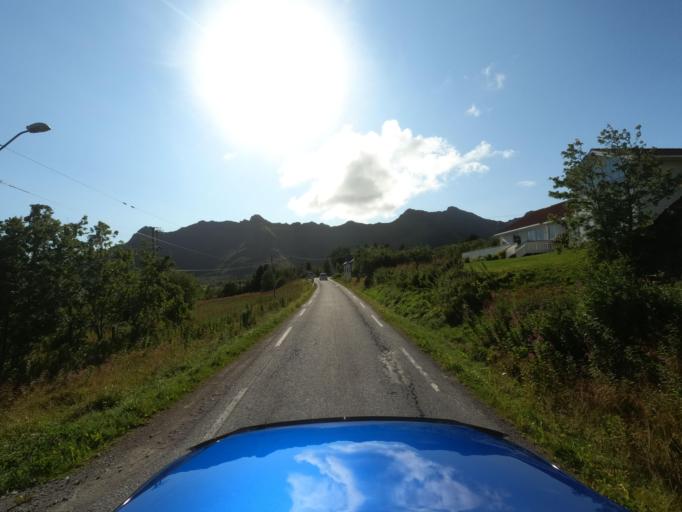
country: NO
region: Nordland
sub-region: Vestvagoy
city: Leknes
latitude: 68.1165
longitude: 13.7117
